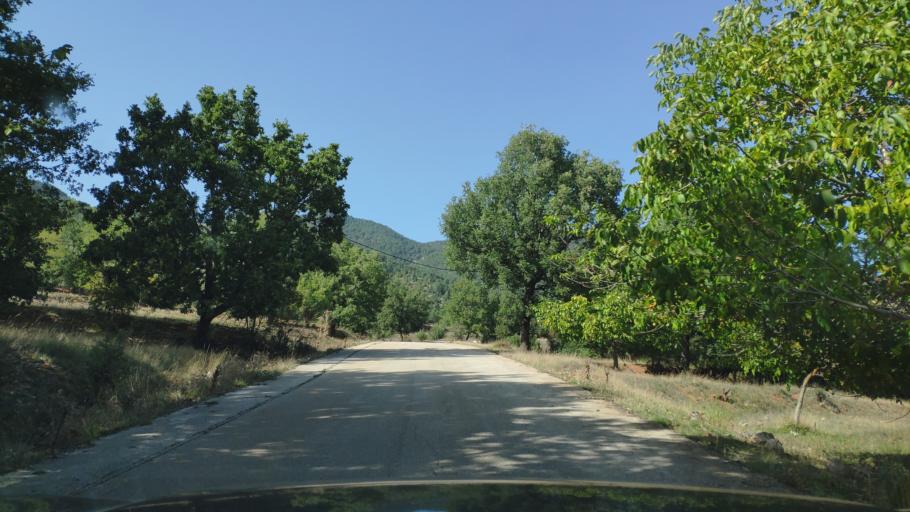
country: GR
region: West Greece
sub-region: Nomos Achaias
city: Aiyira
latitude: 37.9902
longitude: 22.3572
